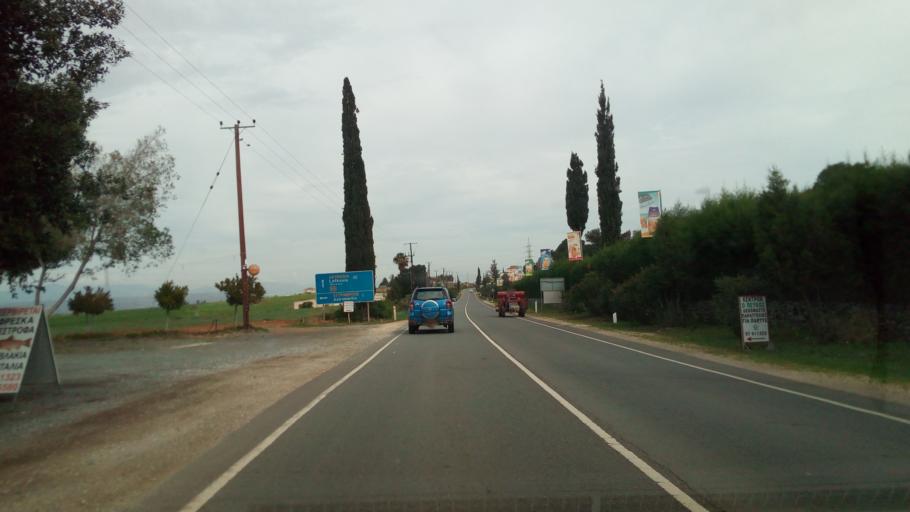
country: CY
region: Lefkosia
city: Astromeritis
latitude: 35.1344
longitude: 33.0205
